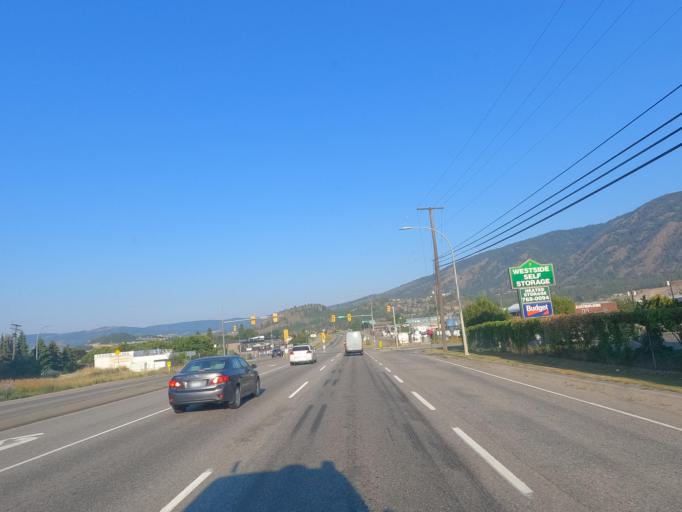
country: CA
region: British Columbia
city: West Kelowna
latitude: 49.8628
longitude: -119.5750
